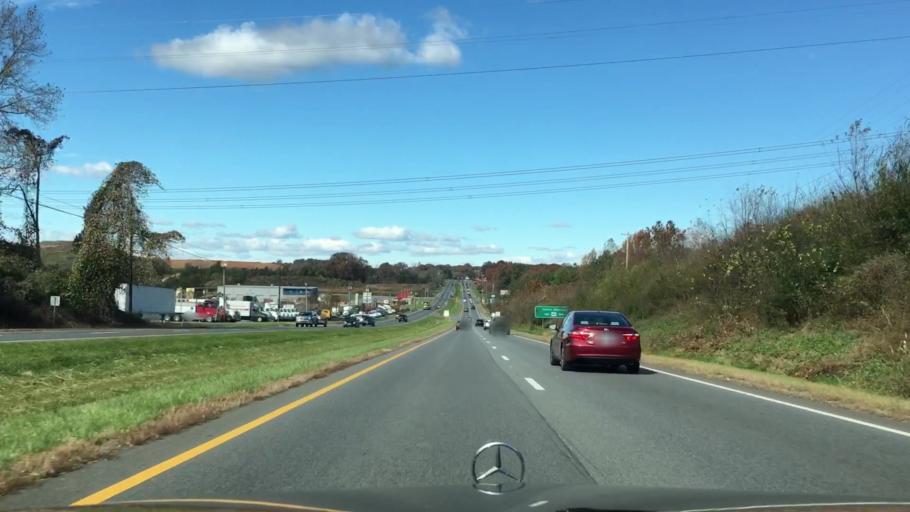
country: US
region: Virginia
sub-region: Campbell County
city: Timberlake
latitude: 37.3071
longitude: -79.1800
